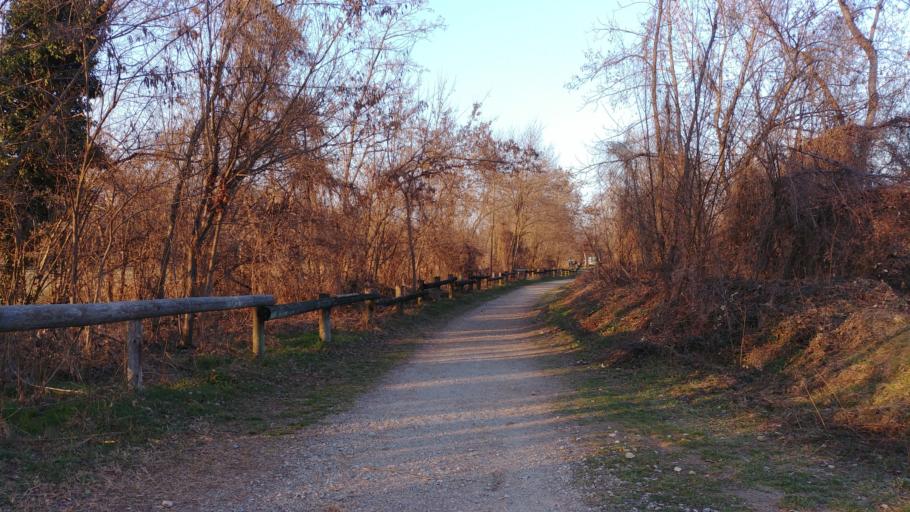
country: IT
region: Piedmont
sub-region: Provincia di Cuneo
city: Cuneo
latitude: 44.3643
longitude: 7.5390
